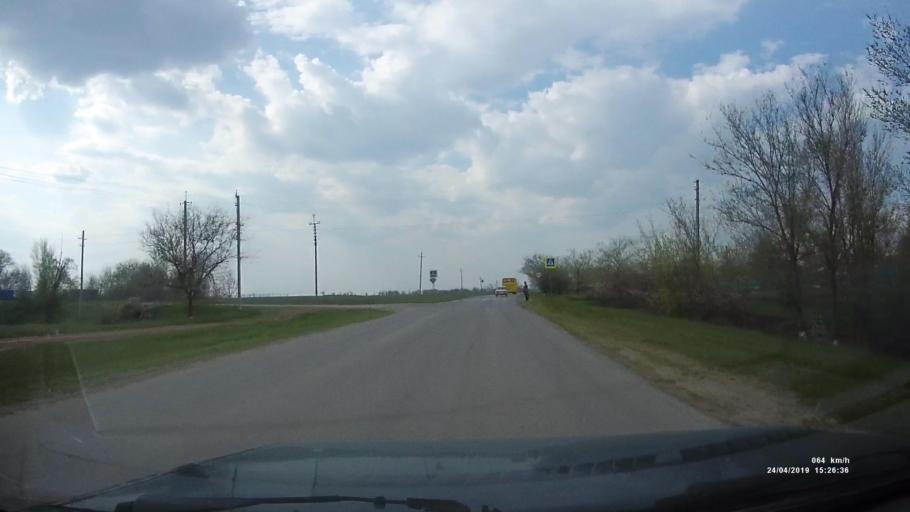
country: RU
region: Rostov
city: Remontnoye
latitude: 46.5588
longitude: 43.0311
